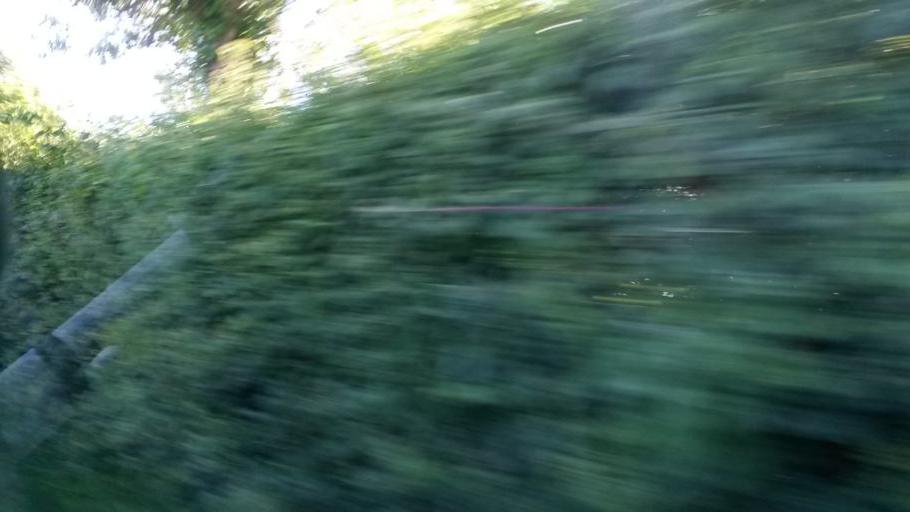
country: IE
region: Leinster
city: Ballymun
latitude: 53.4580
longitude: -6.2963
